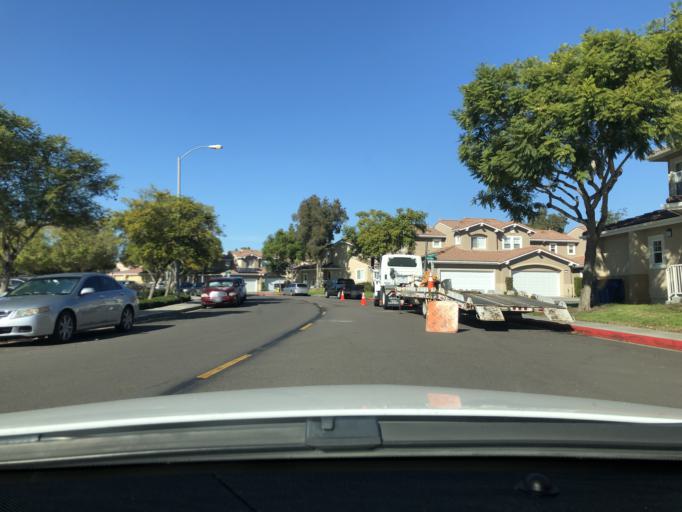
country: US
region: California
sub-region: San Diego County
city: Lemon Grove
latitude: 32.7392
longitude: -117.0592
